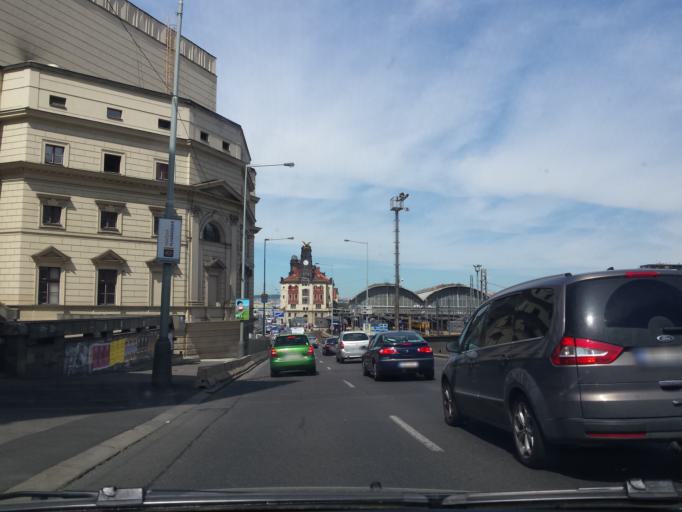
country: CZ
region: Praha
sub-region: Praha 1
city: Stare Mesto
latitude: 50.0799
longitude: 14.4334
